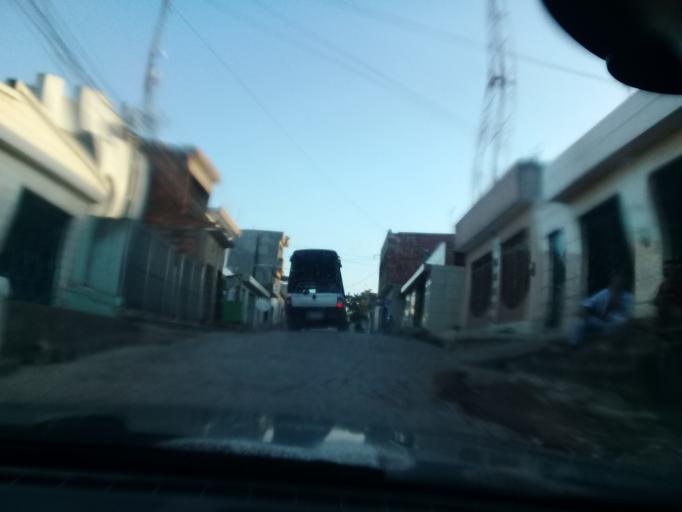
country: BR
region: Pernambuco
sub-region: Vitoria De Santo Antao
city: Vitoria de Santo Antao
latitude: -8.1293
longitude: -35.2869
